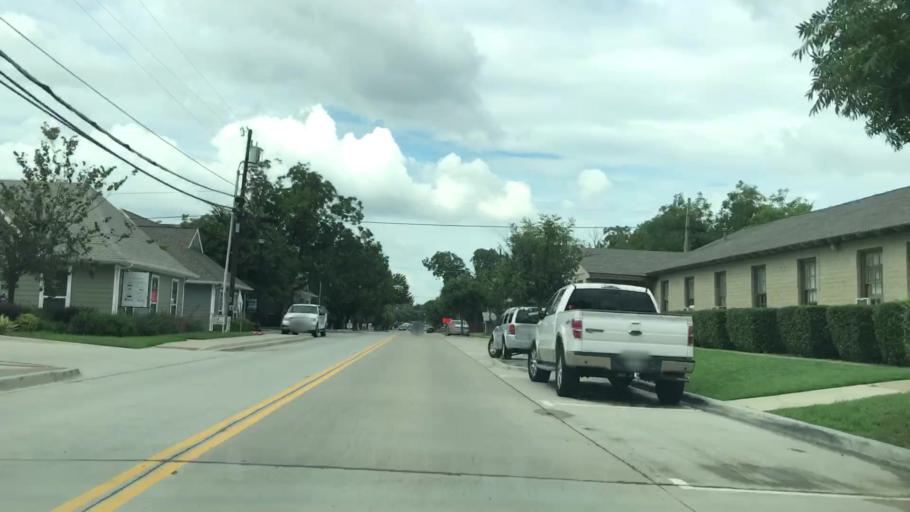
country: US
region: Texas
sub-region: Collin County
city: Frisco
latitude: 33.1477
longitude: -96.8246
